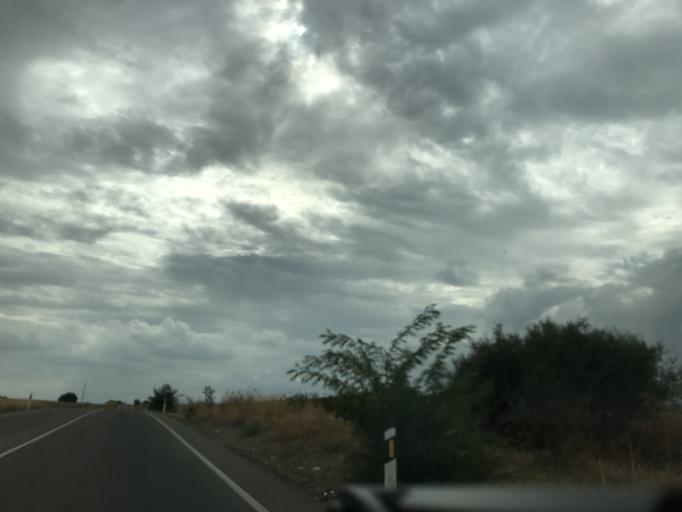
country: ES
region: Andalusia
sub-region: Provincia de Sevilla
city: Tocina
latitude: 37.6385
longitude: -5.7537
